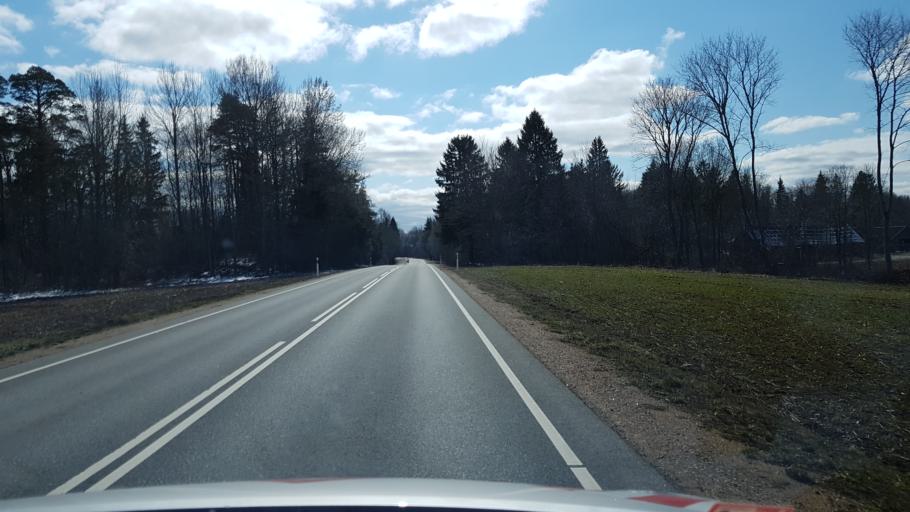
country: EE
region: Laeaene-Virumaa
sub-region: Tapa vald
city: Tapa
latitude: 59.3601
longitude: 26.0002
